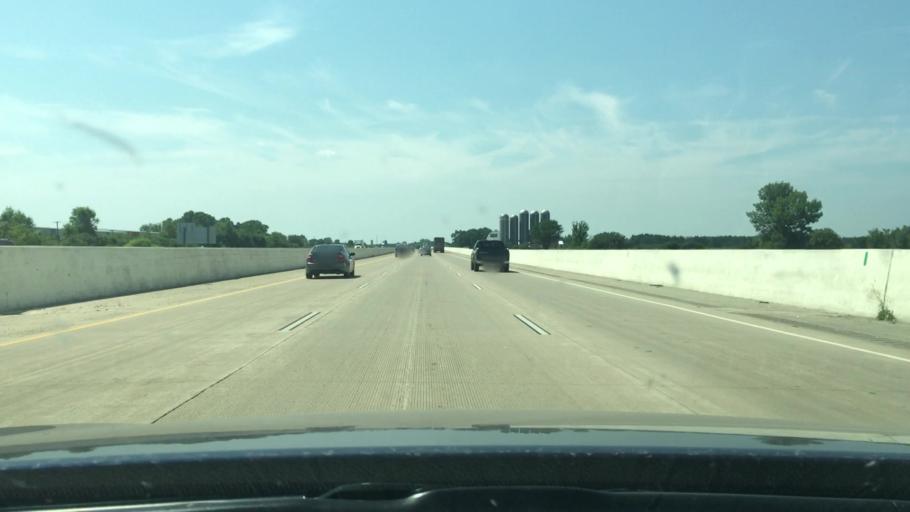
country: US
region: Wisconsin
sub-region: Winnebago County
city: Neenah
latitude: 44.1410
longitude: -88.4913
